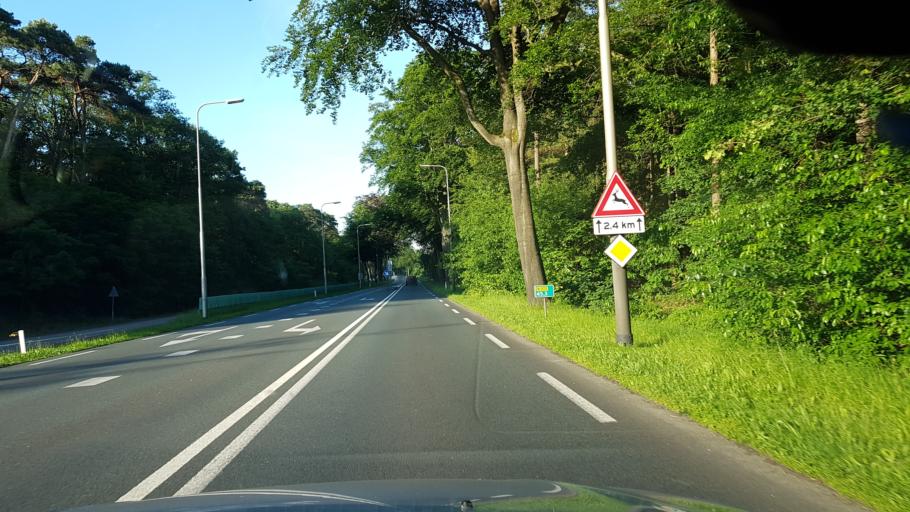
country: NL
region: Limburg
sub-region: Gemeente Maasgouw
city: Maasbracht
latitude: 51.1947
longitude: 5.8825
